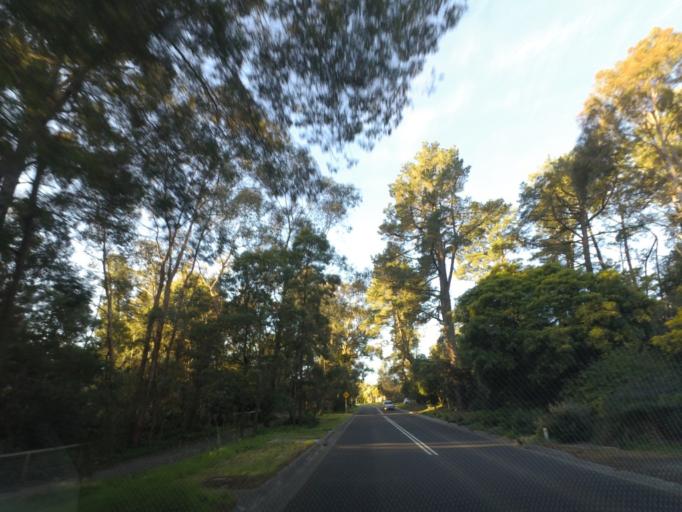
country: AU
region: Victoria
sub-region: Manningham
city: Park Orchards
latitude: -37.7828
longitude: 145.2090
